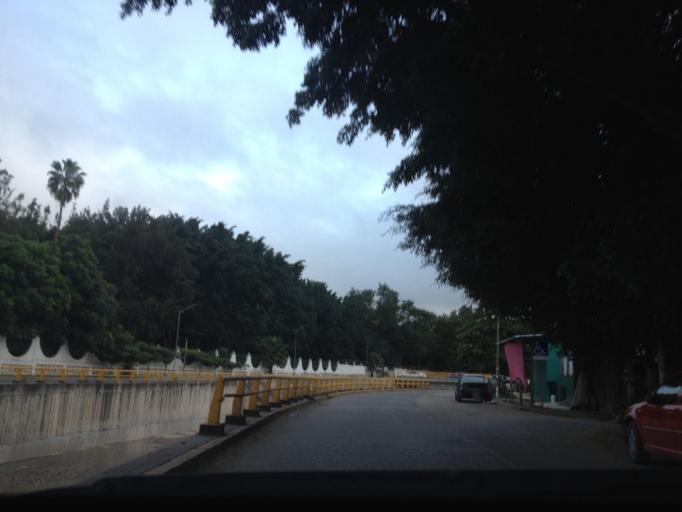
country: MX
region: Guerrero
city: Chilpancingo de los Bravos
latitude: 17.5458
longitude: -99.5021
